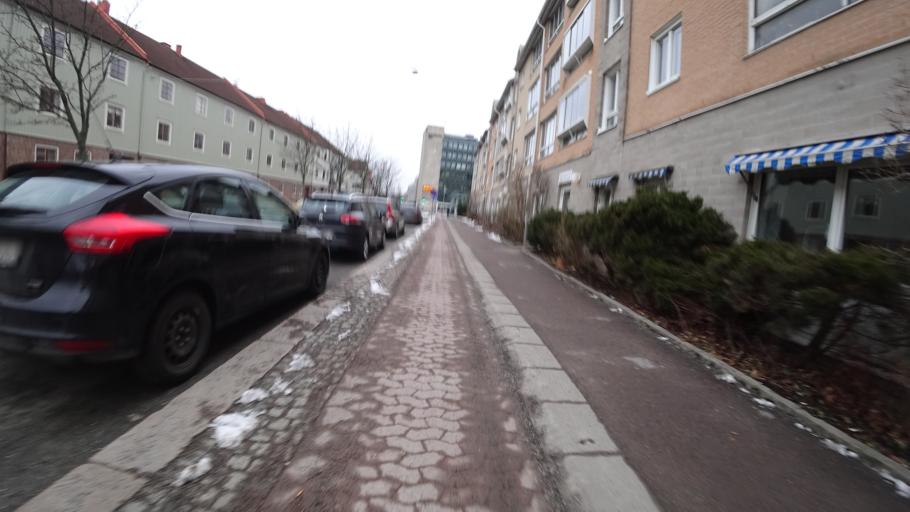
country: SE
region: Vaestra Goetaland
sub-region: Goteborg
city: Majorna
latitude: 57.6886
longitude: 11.9194
